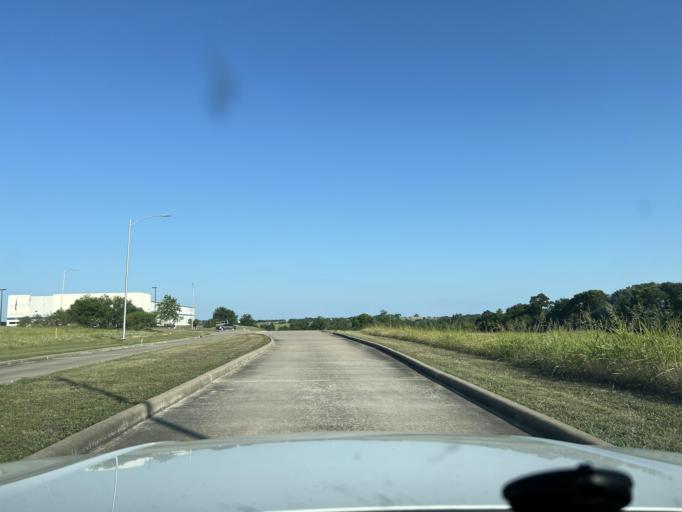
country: US
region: Texas
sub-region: Washington County
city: Brenham
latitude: 30.1382
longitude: -96.3699
